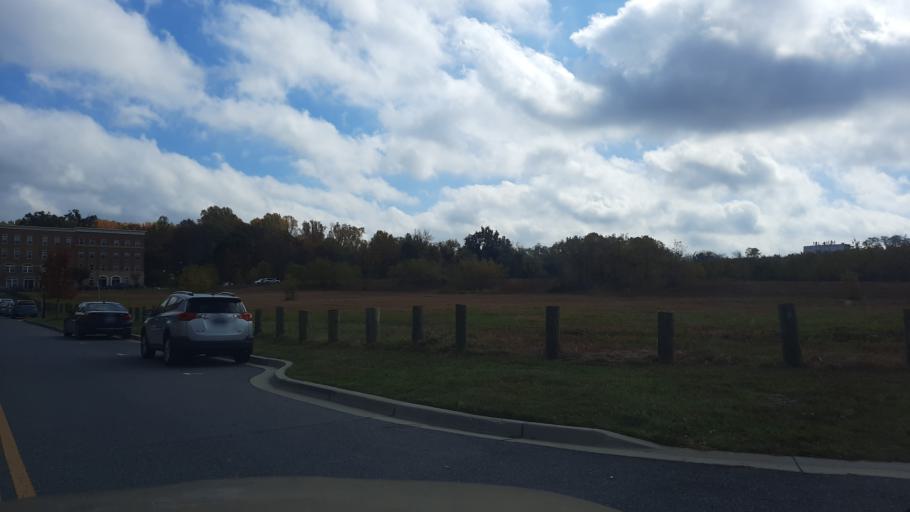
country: US
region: Maryland
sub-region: Montgomery County
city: Gaithersburg
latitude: 39.1522
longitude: -77.2269
